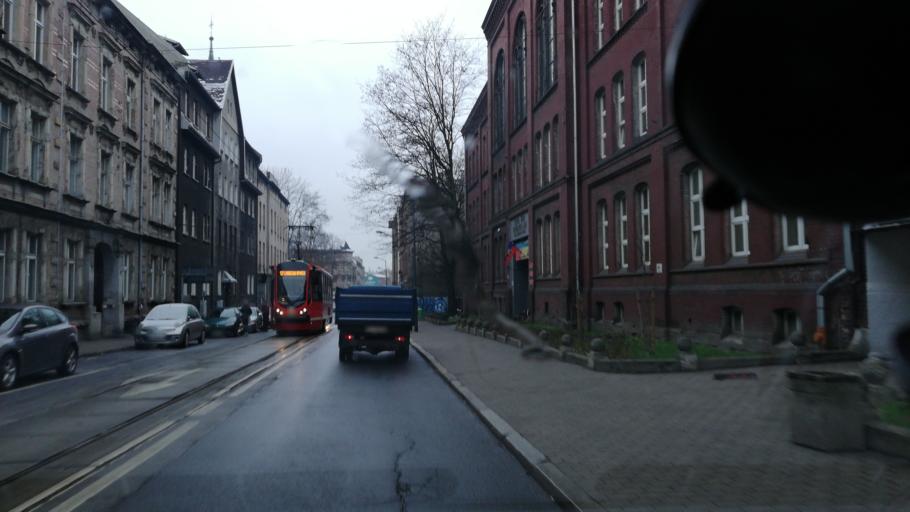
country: PL
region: Silesian Voivodeship
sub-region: Chorzow
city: Chorzow
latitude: 50.2964
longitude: 18.9524
